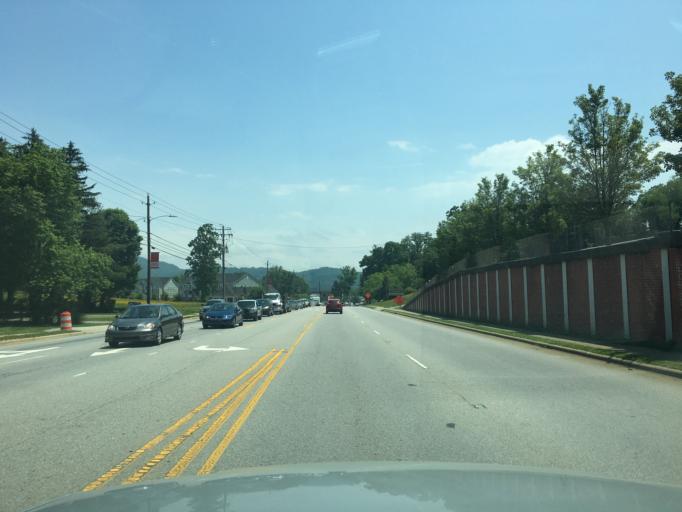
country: US
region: North Carolina
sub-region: Henderson County
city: Fletcher
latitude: 35.4402
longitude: -82.5046
